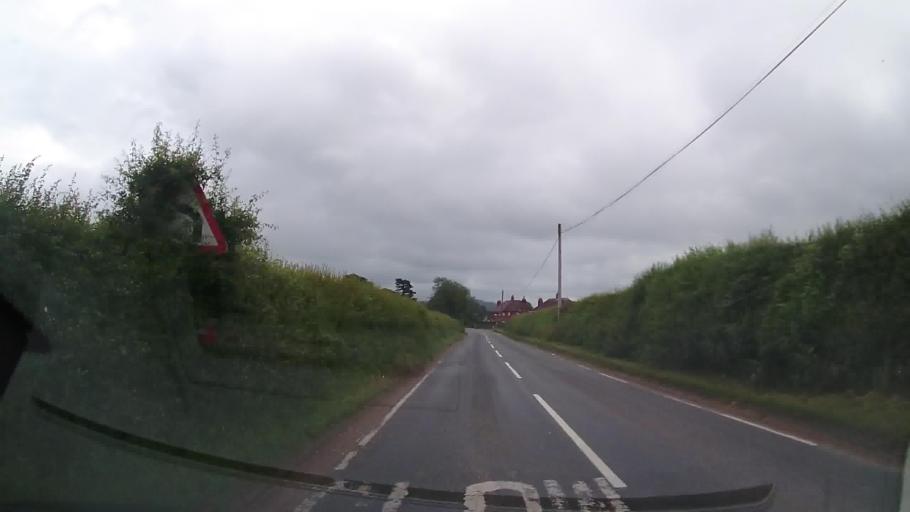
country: GB
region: England
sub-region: Shropshire
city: Wem
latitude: 52.8689
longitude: -2.6853
